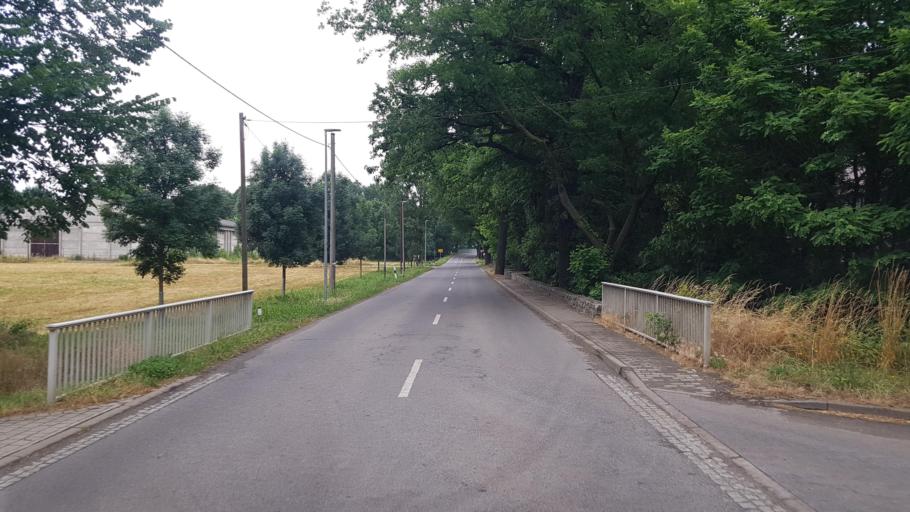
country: DE
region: Brandenburg
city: Schwarzbach
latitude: 51.4753
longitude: 13.9398
